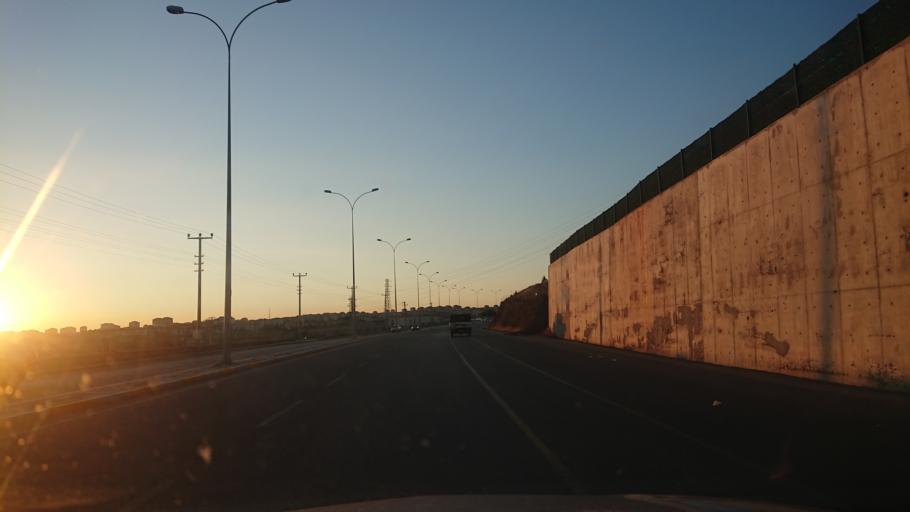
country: TR
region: Aksaray
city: Aksaray
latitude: 38.4044
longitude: 34.0137
